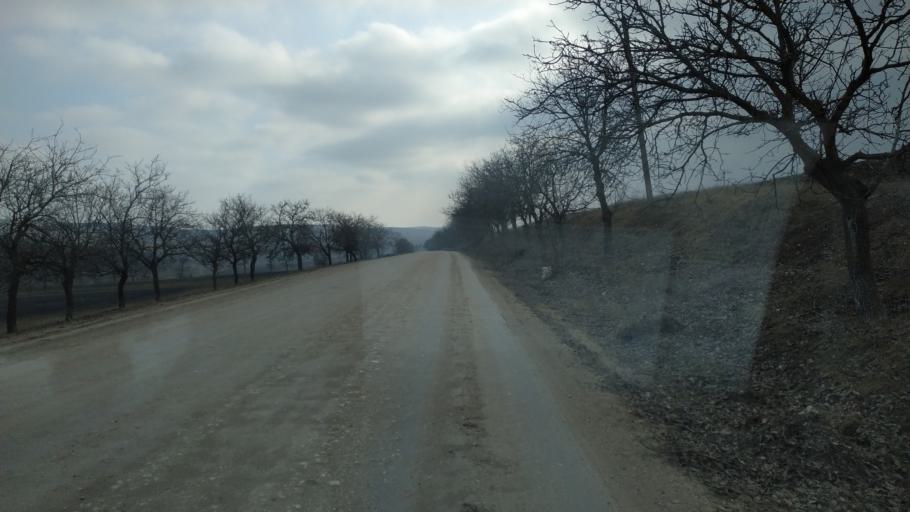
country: MD
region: Hincesti
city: Dancu
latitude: 46.9229
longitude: 28.3282
